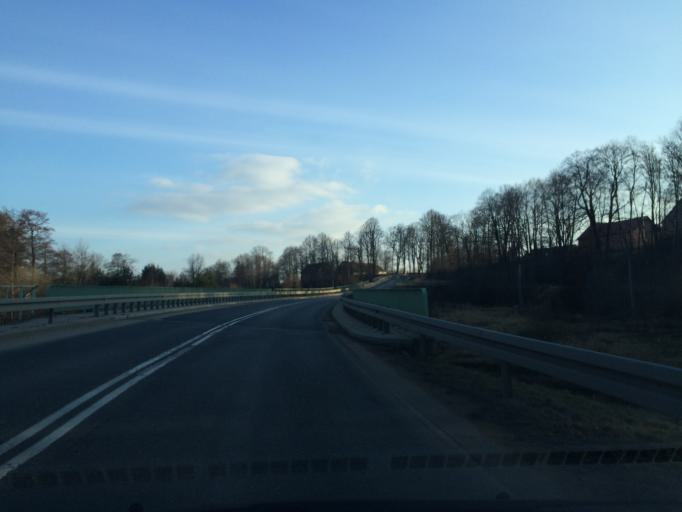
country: PL
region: Lower Silesian Voivodeship
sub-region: Powiat klodzki
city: Bystrzyca Klodzka
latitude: 50.2659
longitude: 16.6618
